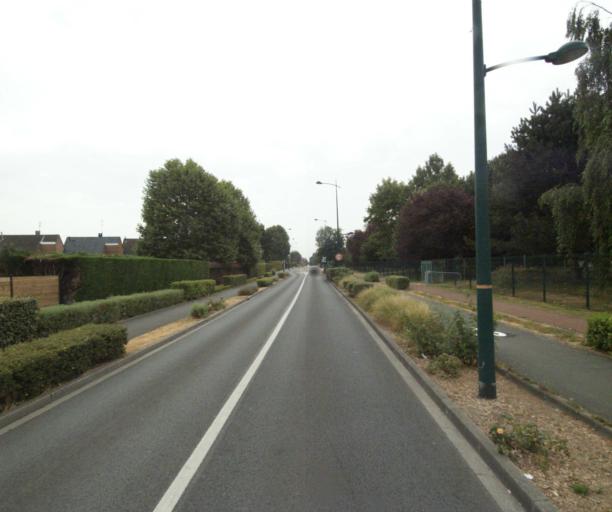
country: FR
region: Nord-Pas-de-Calais
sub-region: Departement du Nord
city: Mouvaux
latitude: 50.7079
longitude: 3.1281
